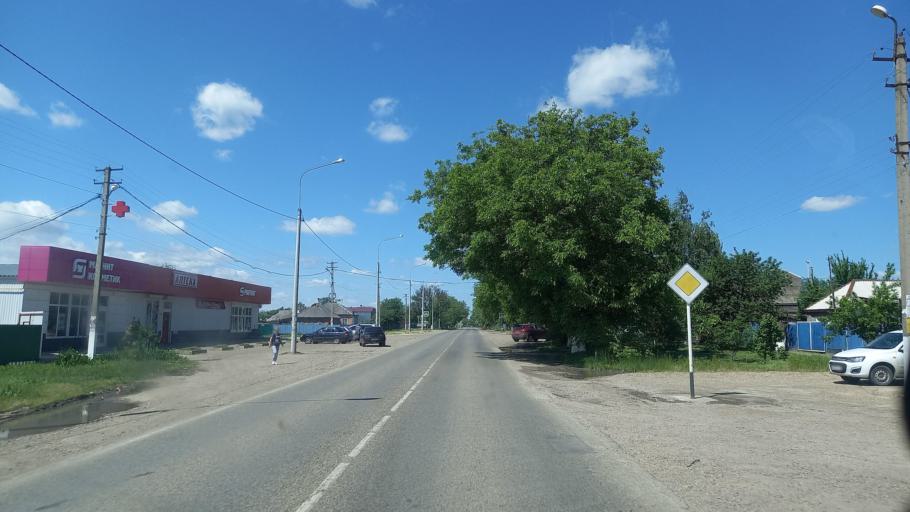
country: RU
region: Krasnodarskiy
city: Novoukrainskoye
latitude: 45.3804
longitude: 40.5122
